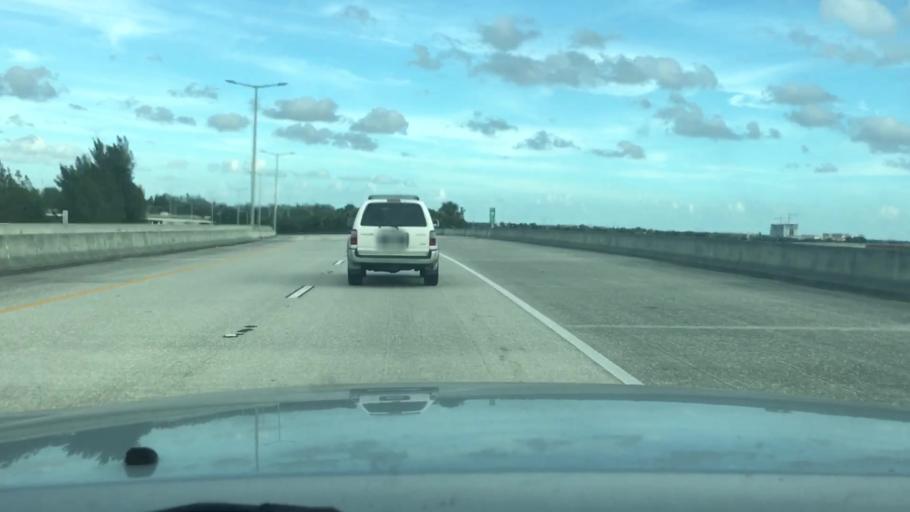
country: US
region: Florida
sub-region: Miami-Dade County
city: Tamiami
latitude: 25.7823
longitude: -80.3912
